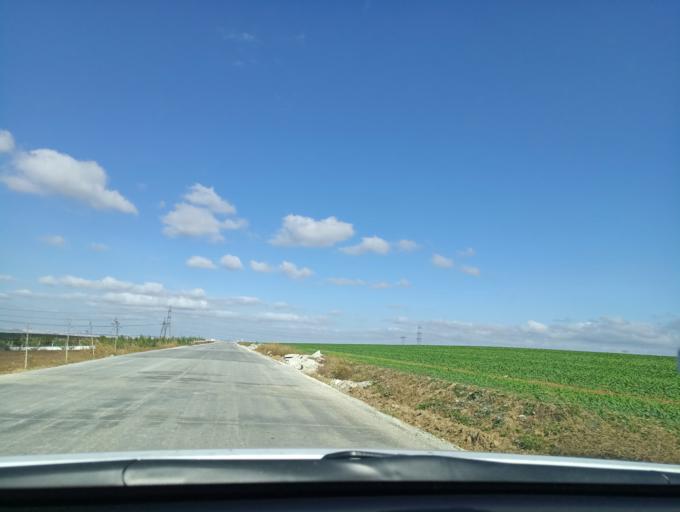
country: TR
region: Tekirdag
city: Corlu
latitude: 41.0537
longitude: 27.8352
